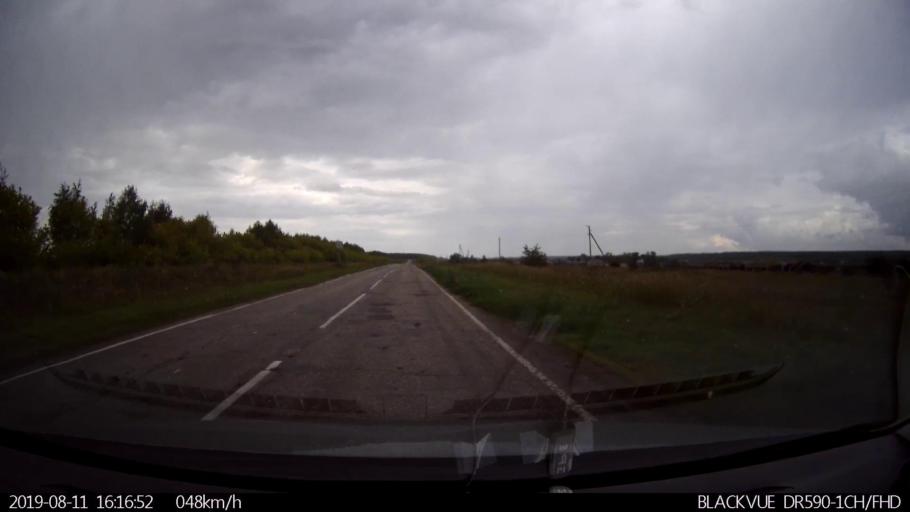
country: RU
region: Ulyanovsk
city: Mayna
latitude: 54.0442
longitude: 47.6193
